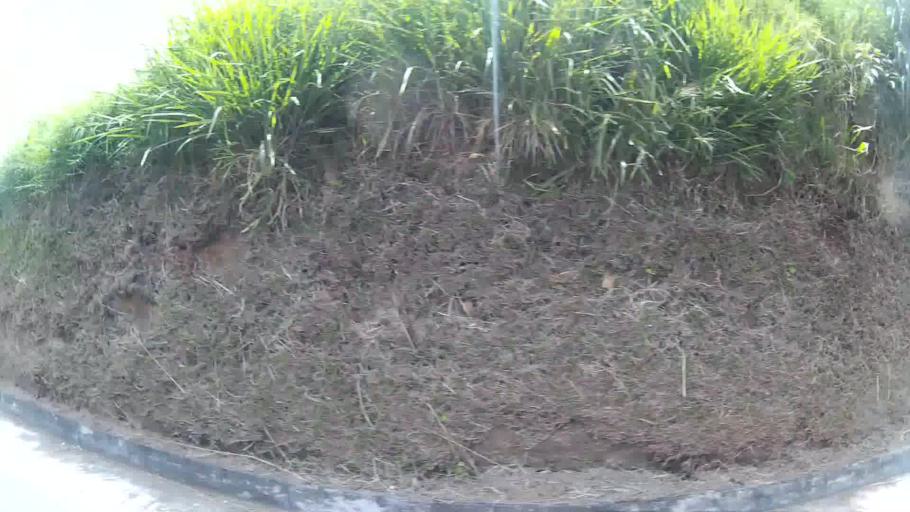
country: CO
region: Risaralda
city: Pereira
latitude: 4.7970
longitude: -75.7551
